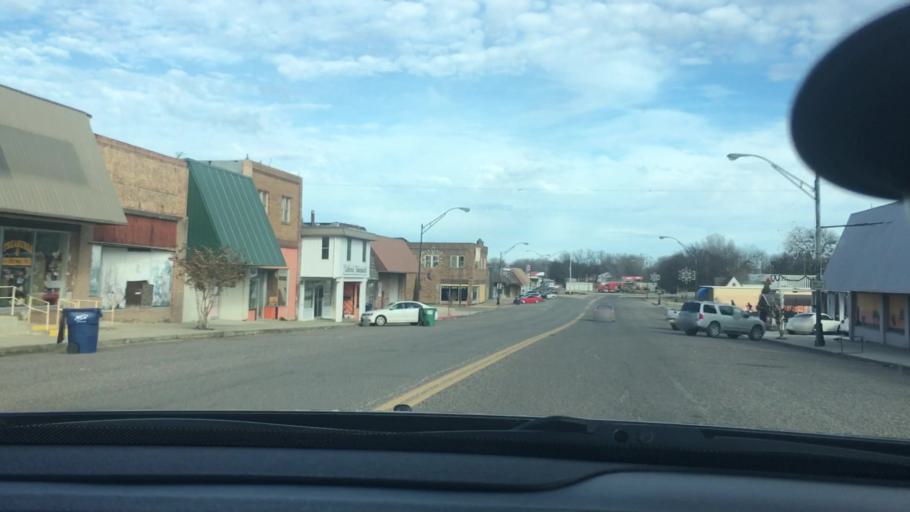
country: US
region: Oklahoma
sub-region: Seminole County
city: Konawa
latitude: 34.9576
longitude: -96.7520
